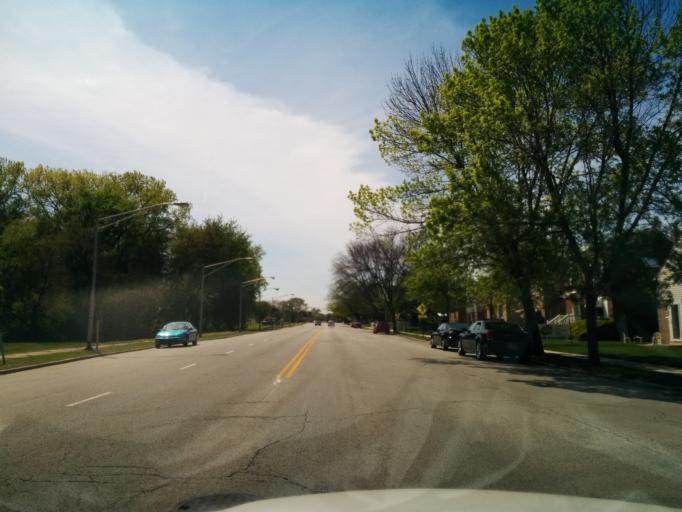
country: US
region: Indiana
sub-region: Lake County
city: Whiting
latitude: 41.6919
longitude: -87.5269
